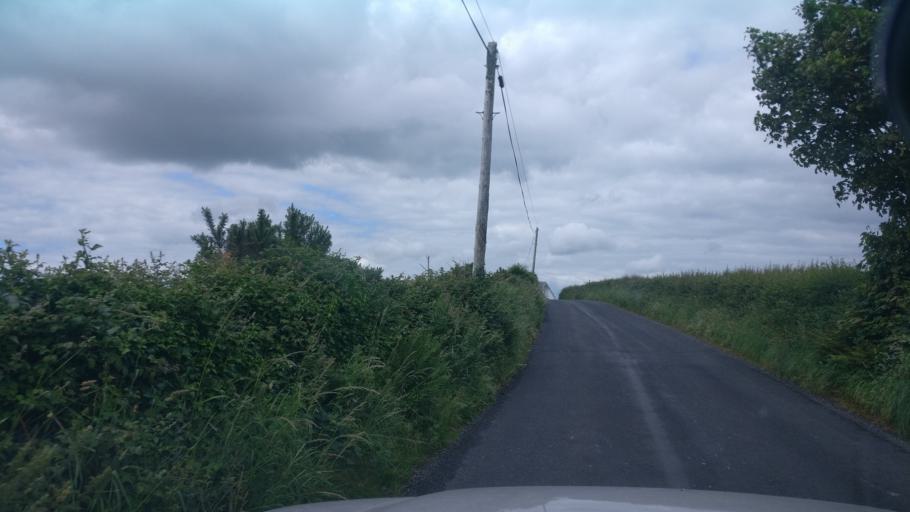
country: IE
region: Connaught
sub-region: County Galway
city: Loughrea
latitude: 53.1670
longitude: -8.5533
